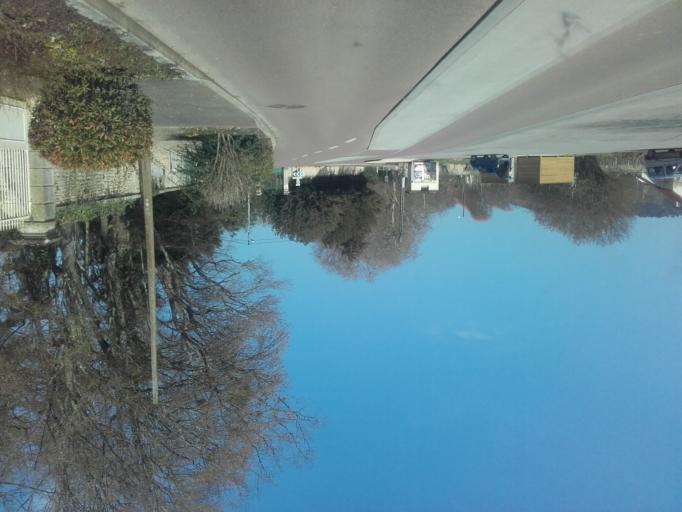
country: FR
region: Bourgogne
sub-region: Departement de la Cote-d'Or
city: Savigny-les-Beaune
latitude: 47.0597
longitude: 4.8256
